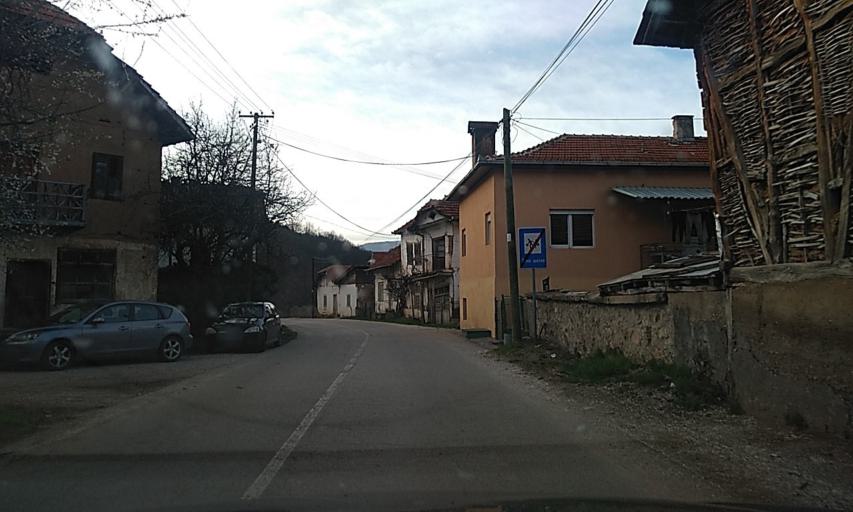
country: RS
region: Central Serbia
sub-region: Pcinjski Okrug
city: Bosilegrad
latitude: 42.4681
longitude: 22.4838
